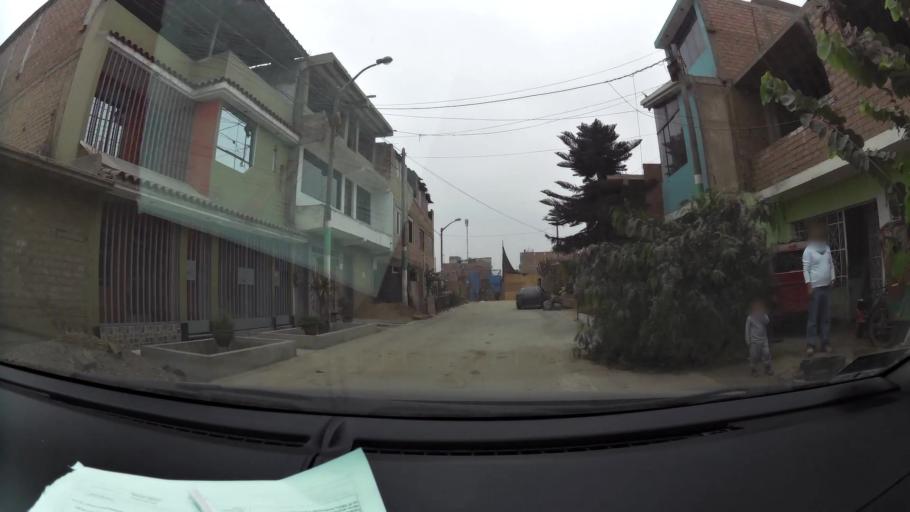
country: PE
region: Lima
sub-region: Lima
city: Urb. Santo Domingo
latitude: -11.8836
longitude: -77.0674
